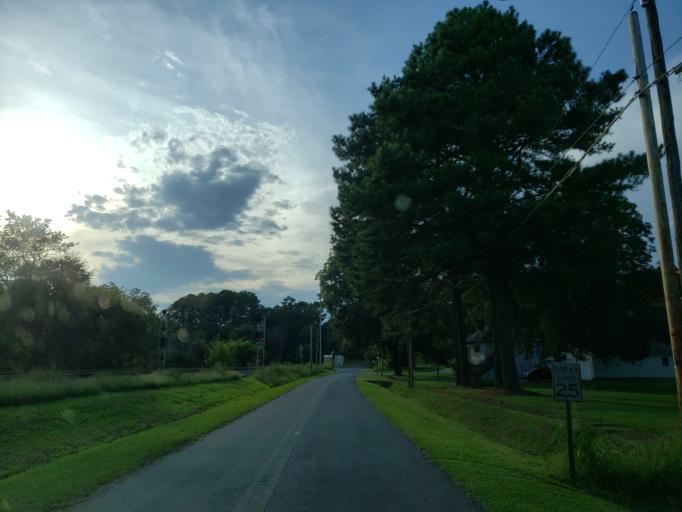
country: US
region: Georgia
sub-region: Bartow County
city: Euharlee
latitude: 34.2376
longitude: -84.9492
